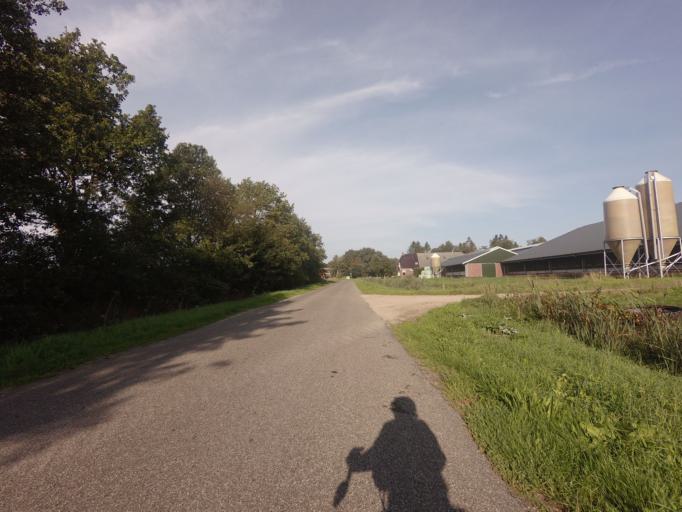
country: NL
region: Groningen
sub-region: Gemeente Leek
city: Leek
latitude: 53.1539
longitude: 6.4345
